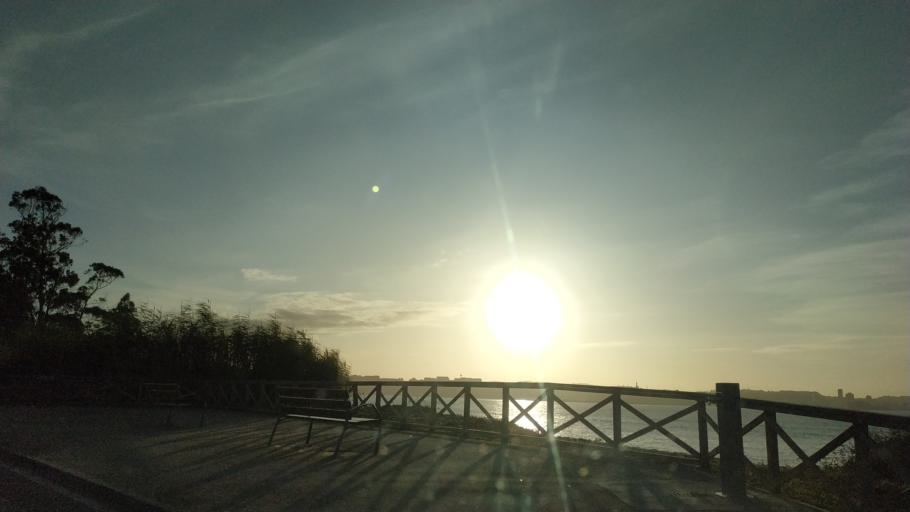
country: ES
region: Galicia
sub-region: Provincia da Coruna
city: Oleiros
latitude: 43.3522
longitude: -8.3472
